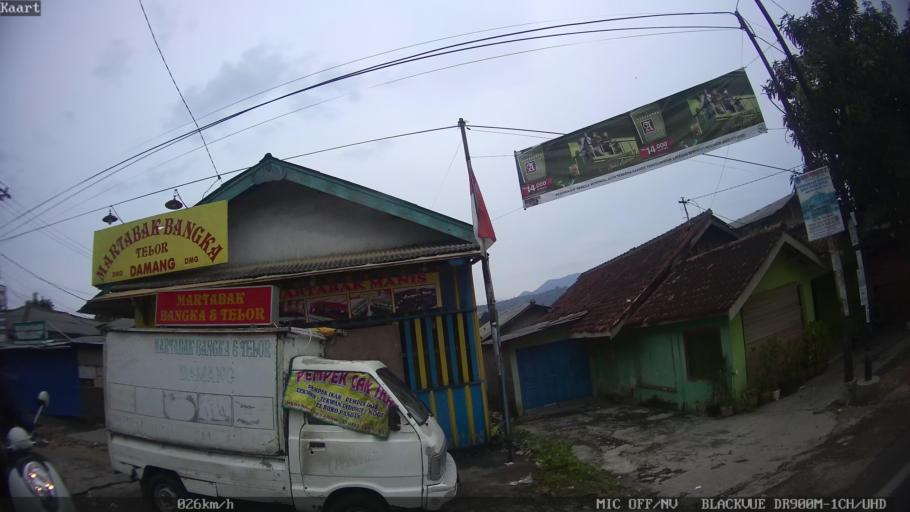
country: ID
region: Lampung
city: Kedaton
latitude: -5.3957
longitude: 105.2368
